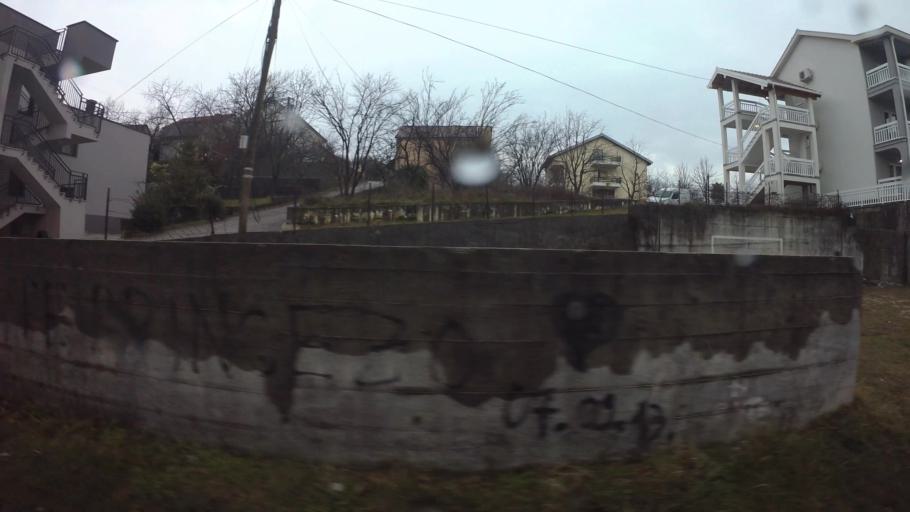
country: BA
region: Federation of Bosnia and Herzegovina
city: Cim
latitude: 43.3508
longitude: 17.7940
